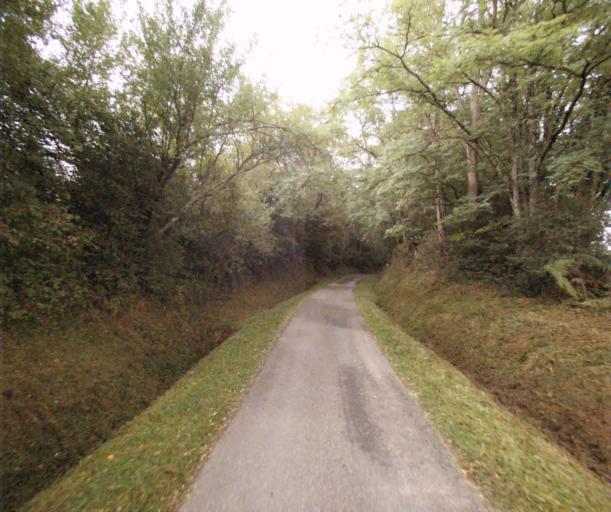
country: FR
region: Midi-Pyrenees
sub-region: Departement du Gers
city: Cazaubon
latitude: 43.9170
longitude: -0.1128
